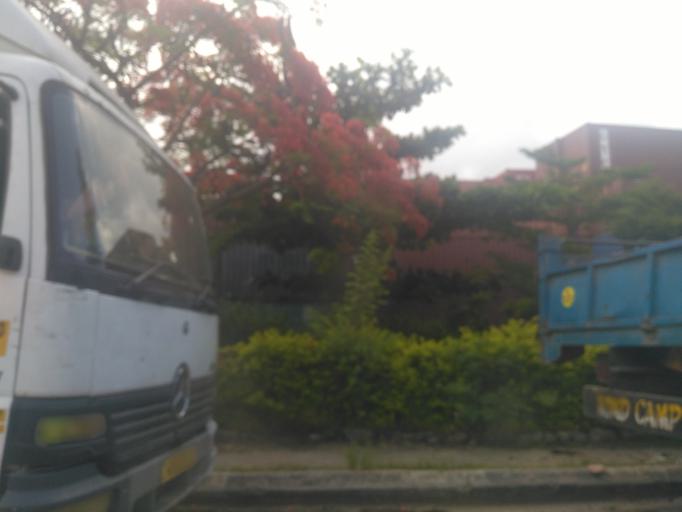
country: TZ
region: Zanzibar Urban/West
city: Zanzibar
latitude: -6.1568
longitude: 39.1966
